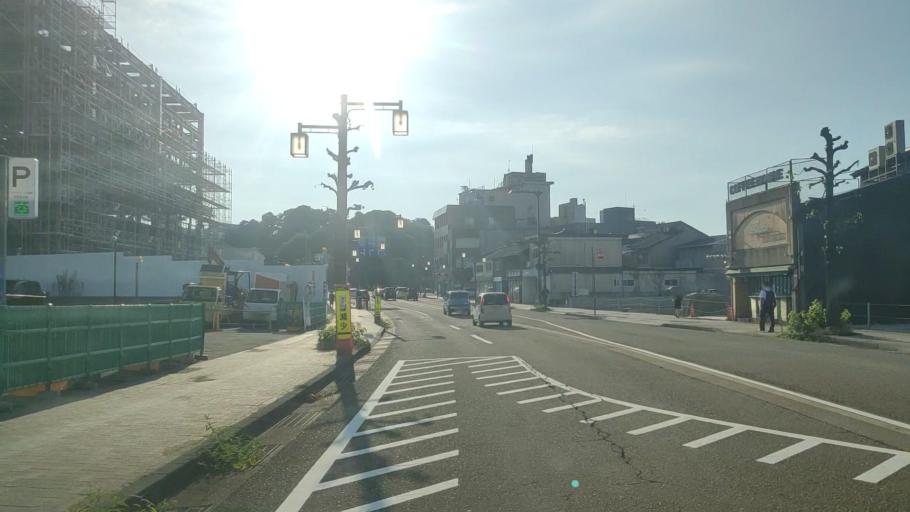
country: JP
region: Ishikawa
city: Kanazawa-shi
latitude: 36.5654
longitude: 136.6649
